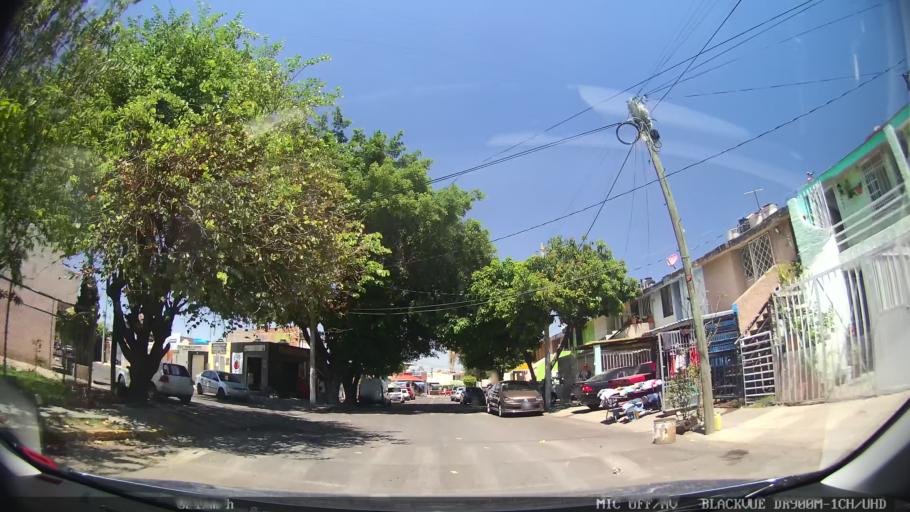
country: MX
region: Jalisco
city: Tlaquepaque
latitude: 20.6829
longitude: -103.2851
